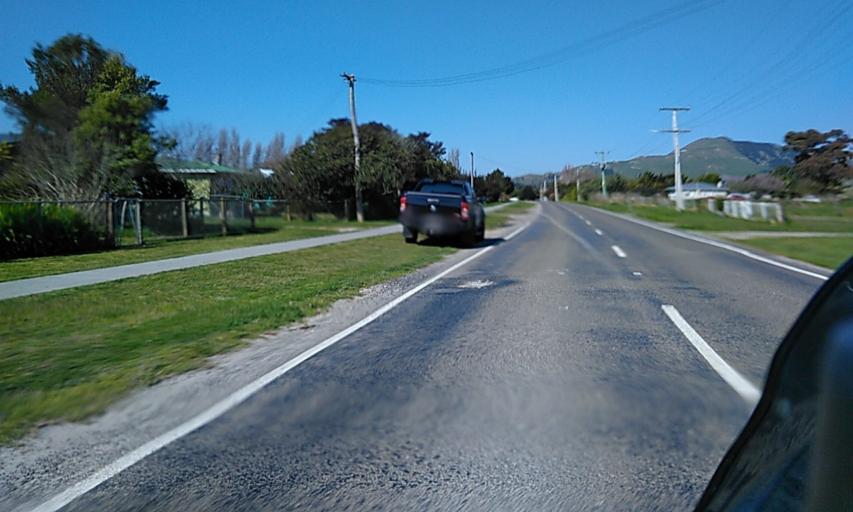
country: NZ
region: Gisborne
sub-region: Gisborne District
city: Gisborne
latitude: -38.3764
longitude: 178.2916
